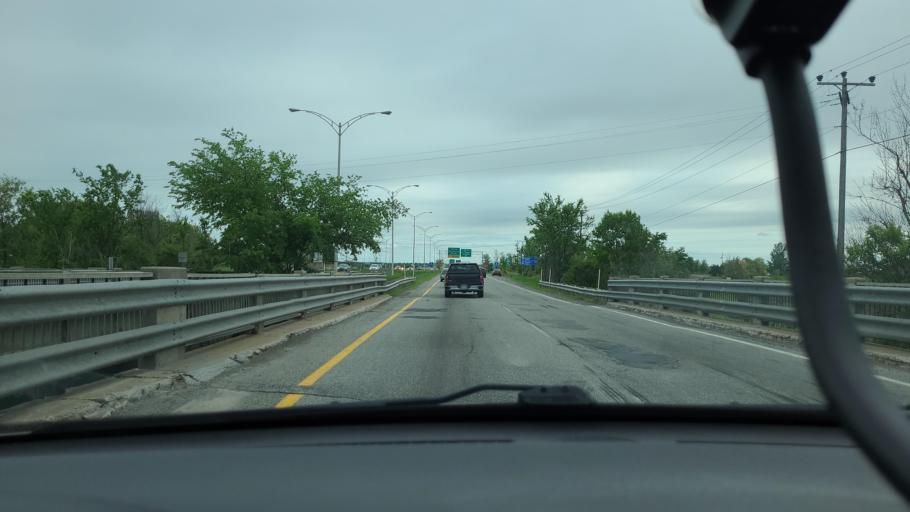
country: CA
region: Quebec
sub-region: Lanaudiere
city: Sainte-Julienne
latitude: 45.8977
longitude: -73.6596
